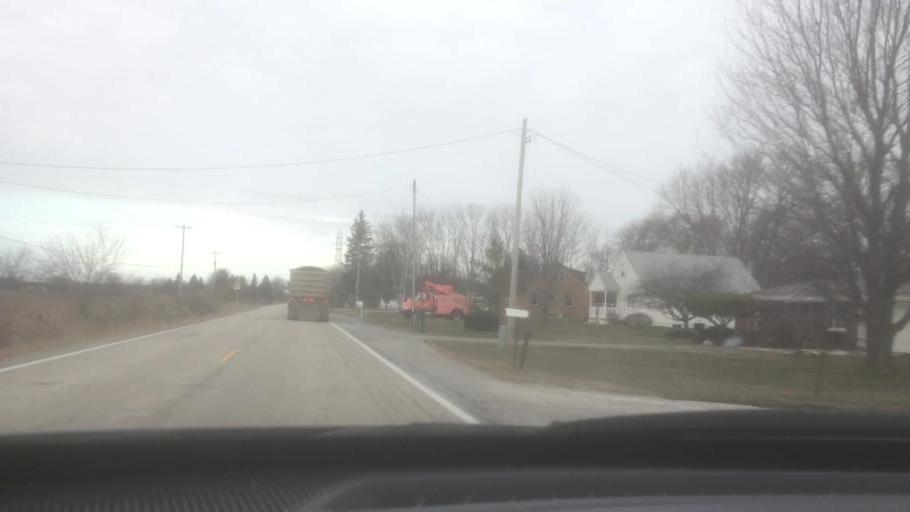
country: US
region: Michigan
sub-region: Bay County
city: Essexville
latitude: 43.5221
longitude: -83.7880
